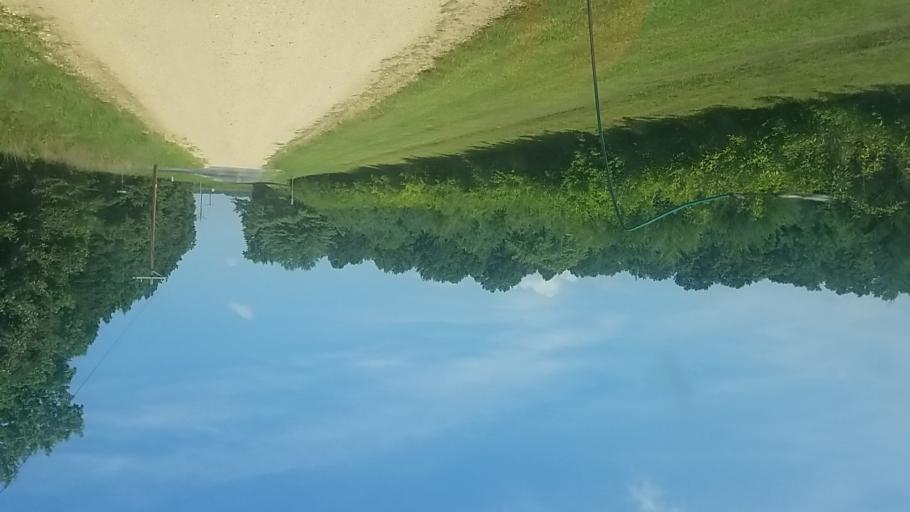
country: US
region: Maryland
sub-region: Caroline County
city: Denton
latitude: 38.8712
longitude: -75.7466
